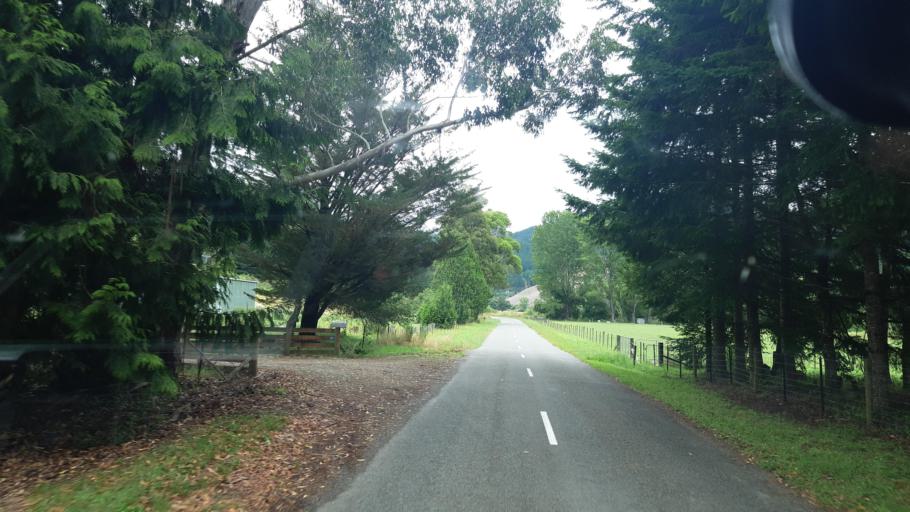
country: NZ
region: Marlborough
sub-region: Marlborough District
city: Blenheim
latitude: -41.4517
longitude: 173.7177
